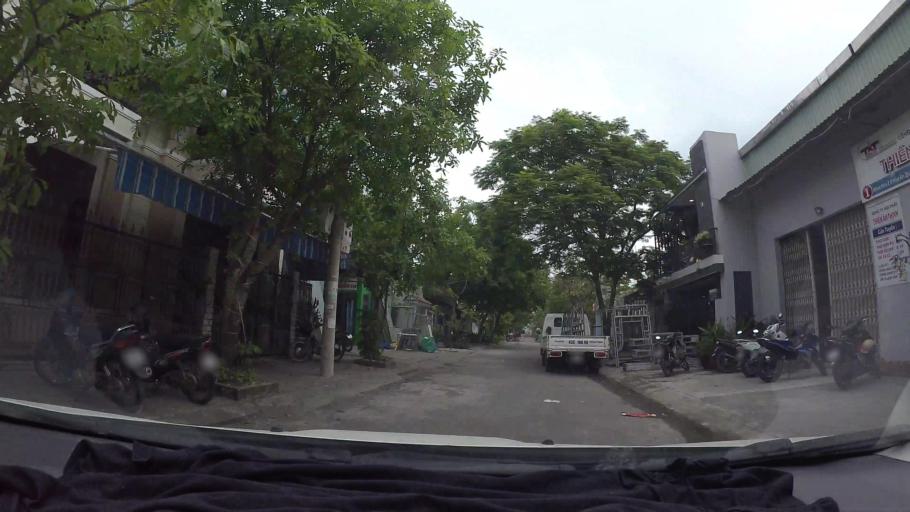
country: VN
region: Da Nang
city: Thanh Khe
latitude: 16.0471
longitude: 108.1736
